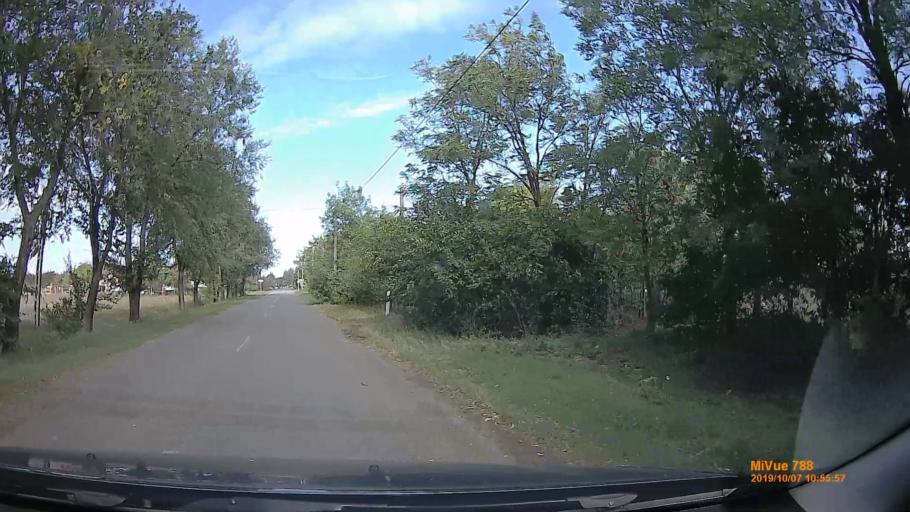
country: HU
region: Bekes
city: Kondoros
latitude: 46.7459
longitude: 20.8034
